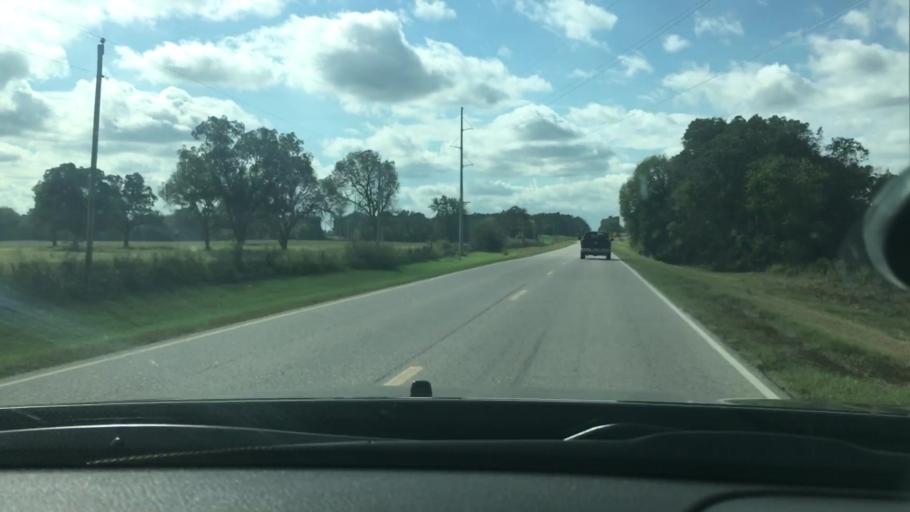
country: US
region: Oklahoma
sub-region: Pontotoc County
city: Ada
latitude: 34.7077
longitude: -96.6349
